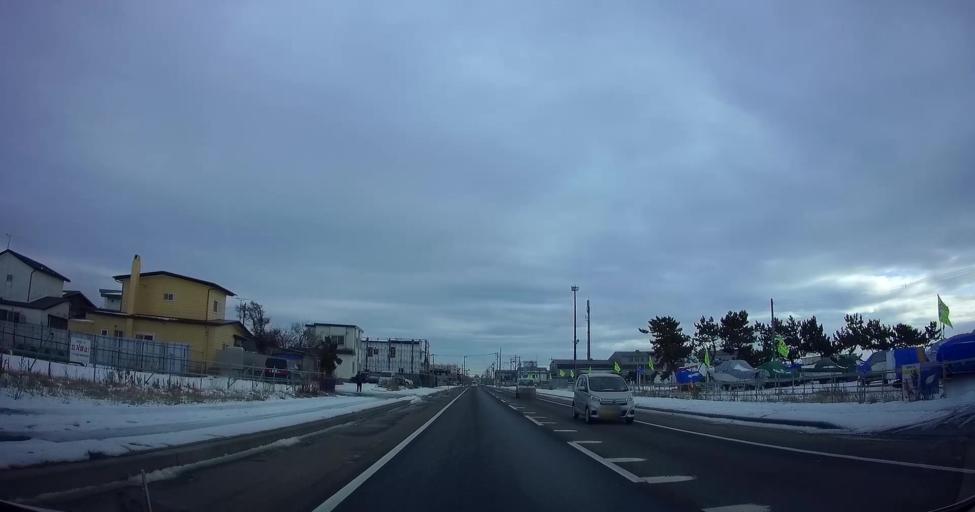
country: JP
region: Hokkaido
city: Hakodate
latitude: 41.8148
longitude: 140.7034
